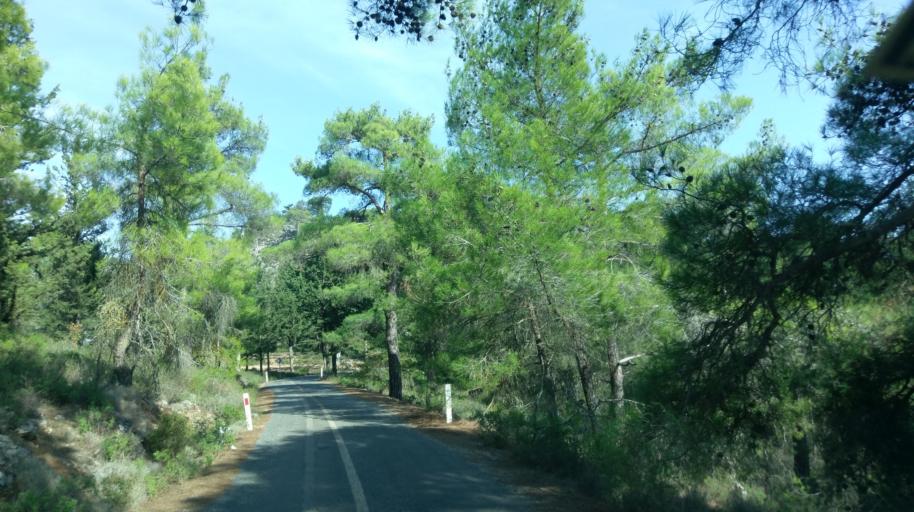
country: CY
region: Keryneia
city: Kyrenia
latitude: 35.3074
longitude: 33.2542
